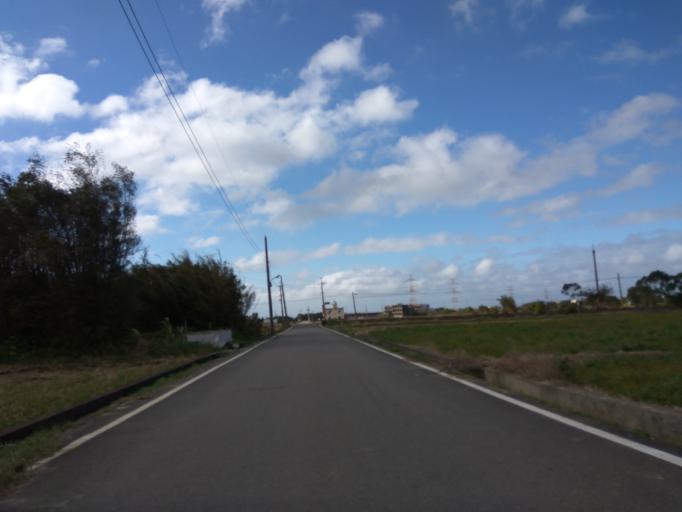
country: TW
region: Taiwan
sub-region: Hsinchu
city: Zhubei
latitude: 24.9713
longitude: 121.0801
